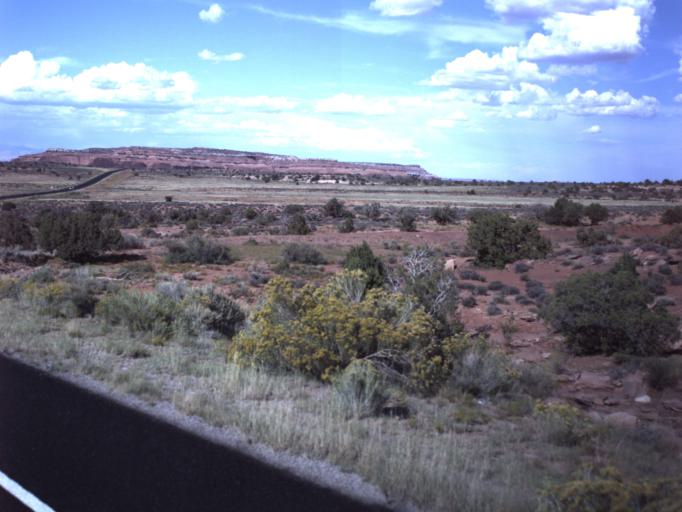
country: US
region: Utah
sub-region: Grand County
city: Moab
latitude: 38.6092
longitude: -109.8172
